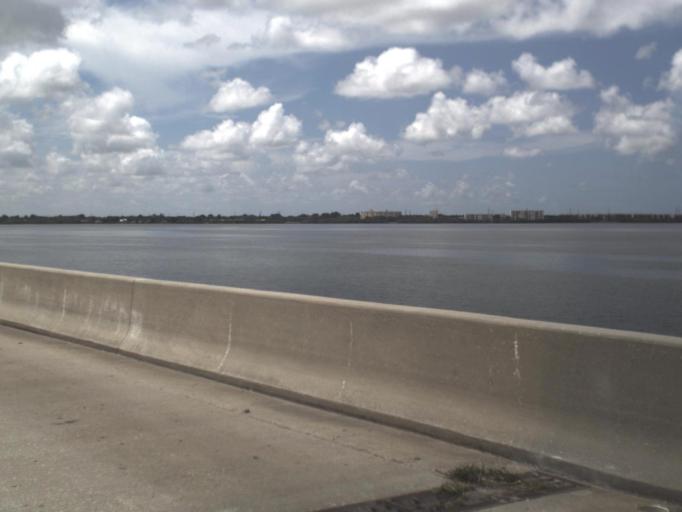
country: US
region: Florida
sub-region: Pinellas County
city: South Highpoint
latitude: 27.9531
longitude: -82.7074
